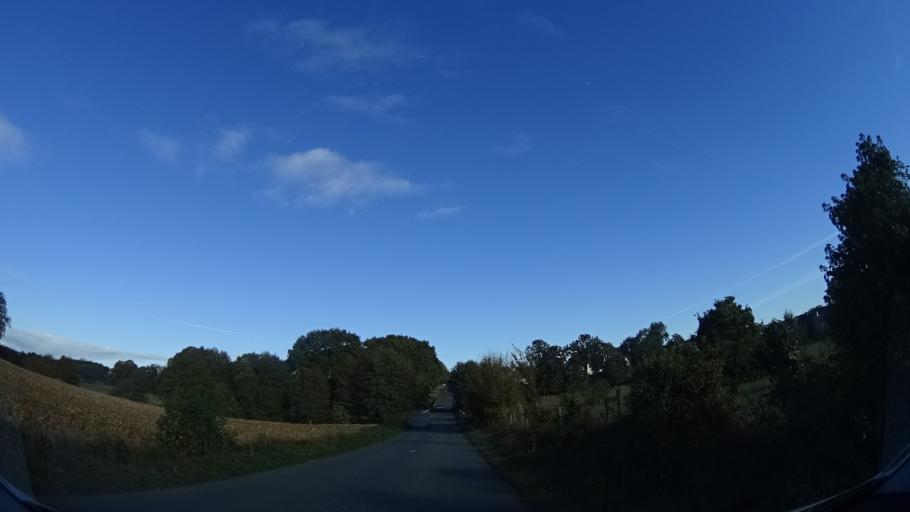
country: FR
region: Brittany
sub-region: Departement d'Ille-et-Vilaine
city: Geveze
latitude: 48.2131
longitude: -1.7913
